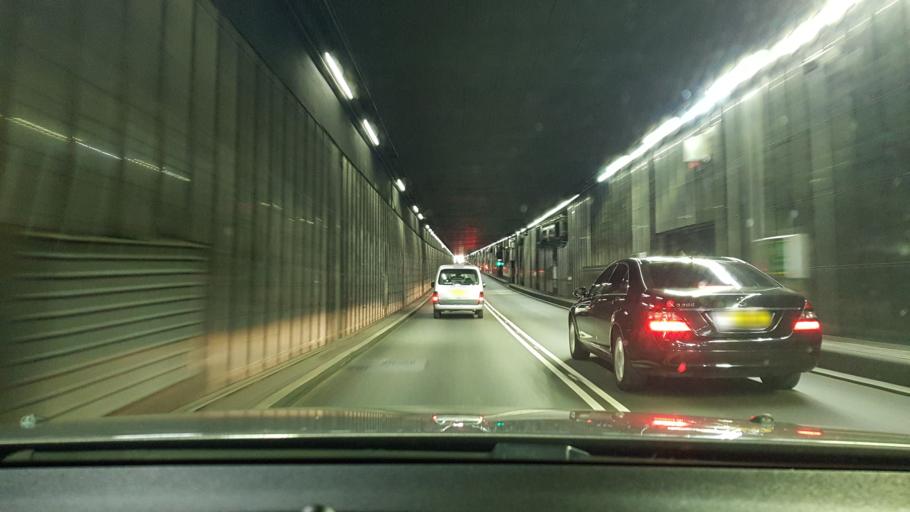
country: GB
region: England
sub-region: Greater London
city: West Drayton
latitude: 51.4743
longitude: -0.4530
